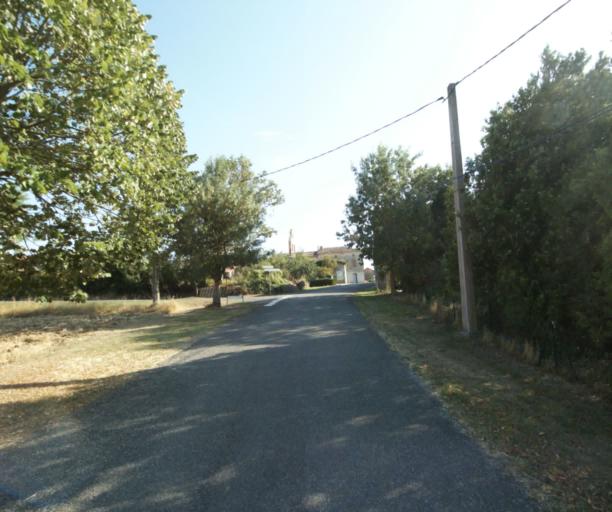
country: FR
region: Midi-Pyrenees
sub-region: Departement de la Haute-Garonne
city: Saint-Felix-Lauragais
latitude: 43.4422
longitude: 1.8228
